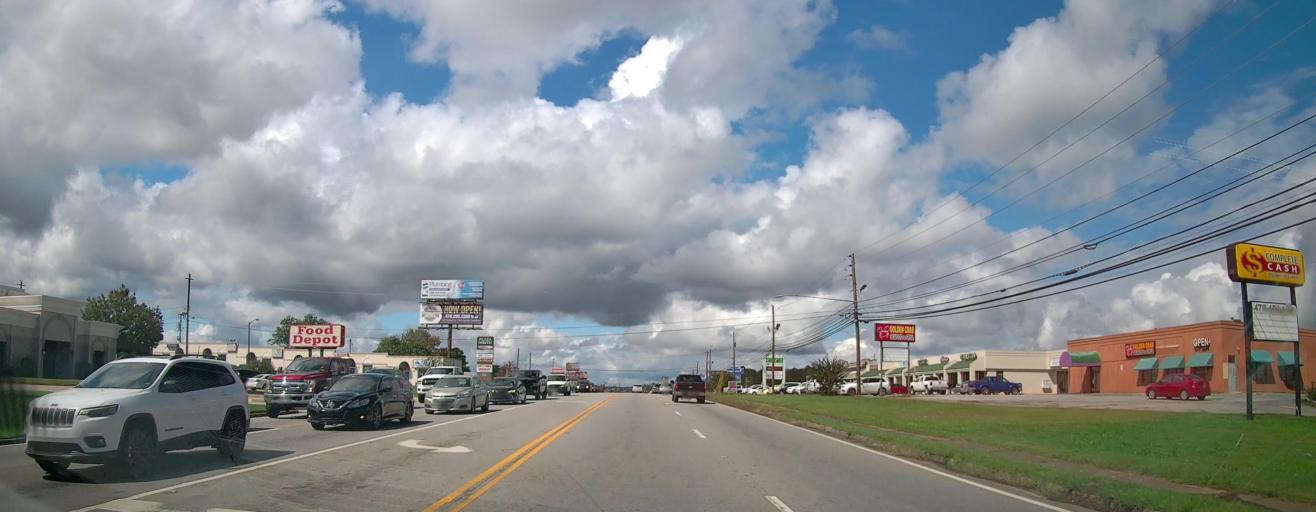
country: US
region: Georgia
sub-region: Baldwin County
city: Milledgeville
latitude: 33.1019
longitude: -83.2485
